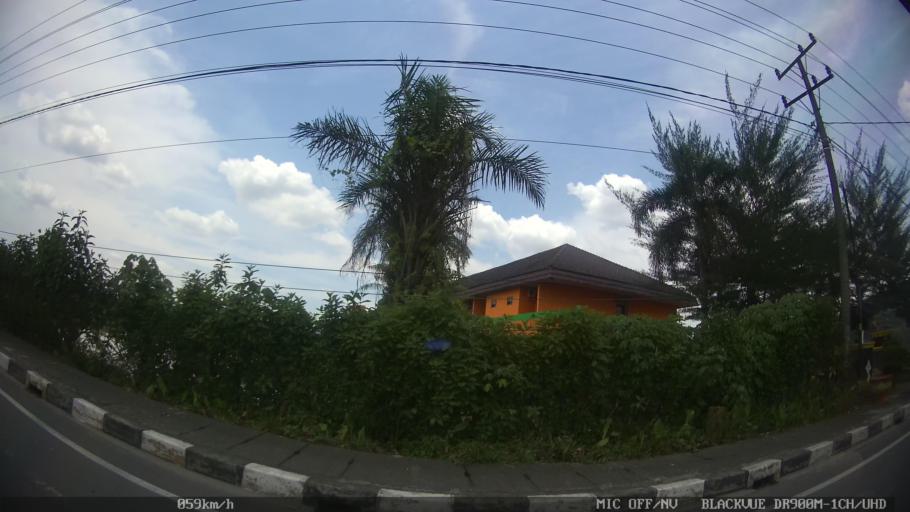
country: ID
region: North Sumatra
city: Binjai
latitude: 3.6044
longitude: 98.5312
